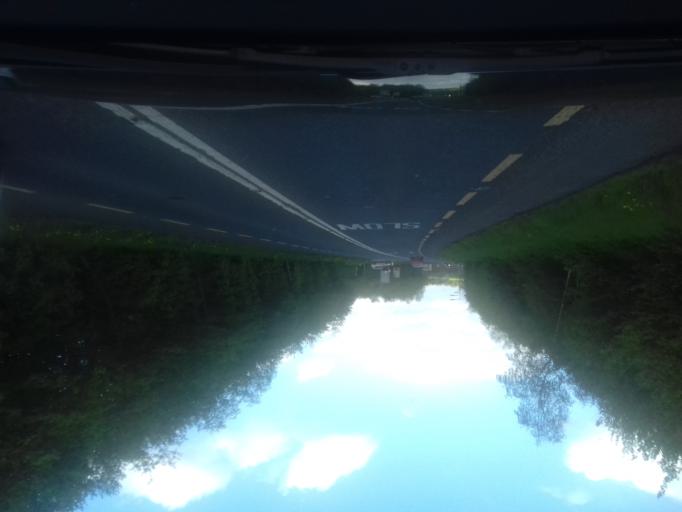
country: IE
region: Leinster
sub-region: Laois
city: Portlaoise
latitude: 53.0462
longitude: -7.2481
